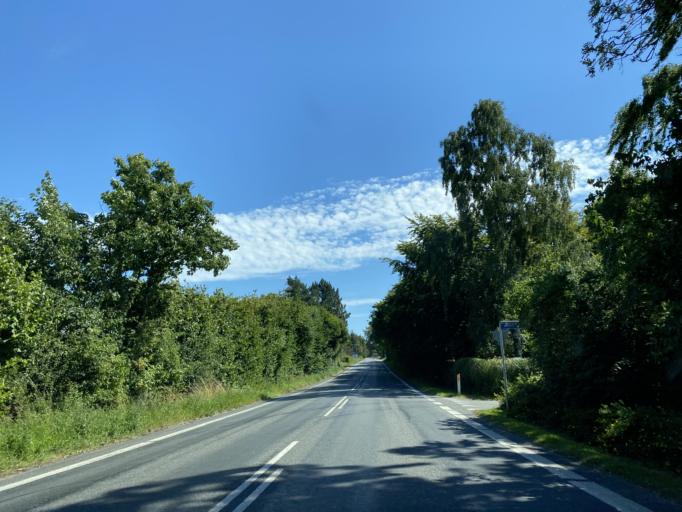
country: DK
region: South Denmark
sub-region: Odense Kommune
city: Bellinge
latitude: 55.2097
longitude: 10.3377
